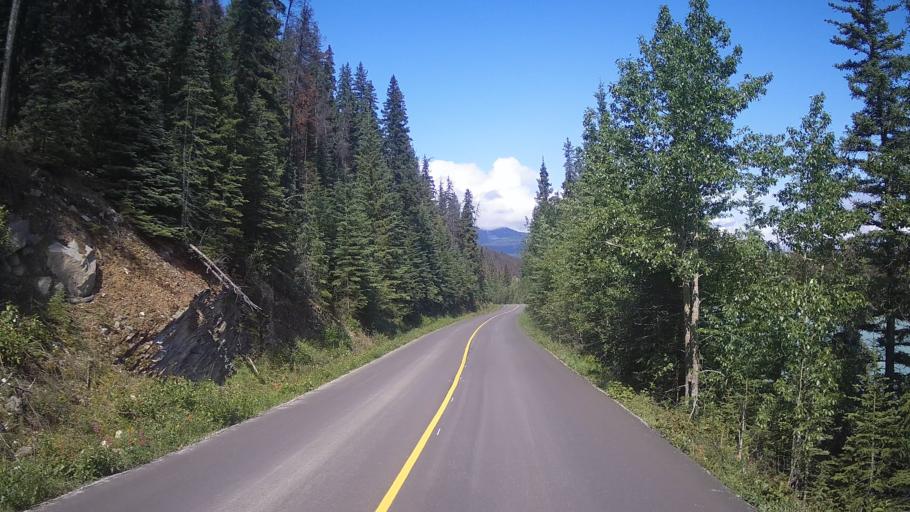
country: CA
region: Alberta
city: Jasper Park Lodge
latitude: 52.7401
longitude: -117.9614
